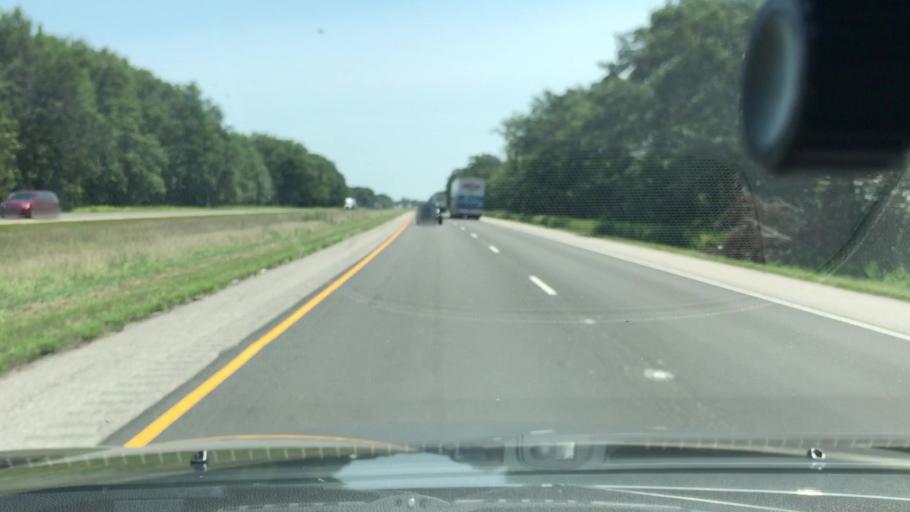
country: US
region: Illinois
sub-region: Clinton County
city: Wamac
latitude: 38.3876
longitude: -89.1556
